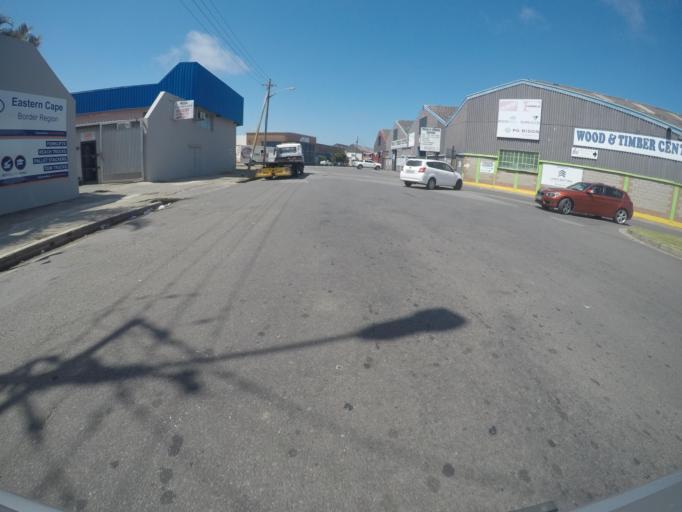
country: ZA
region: Eastern Cape
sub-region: Buffalo City Metropolitan Municipality
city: East London
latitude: -33.0085
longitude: 27.9092
